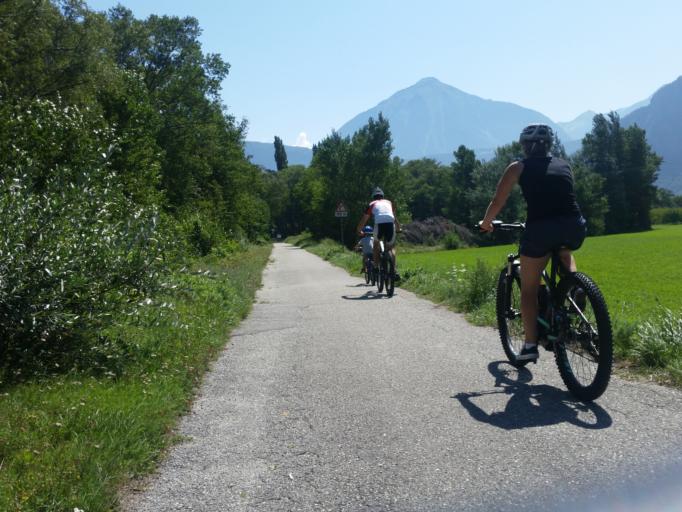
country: CH
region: Valais
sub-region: Saint-Maurice District
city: Vernayaz
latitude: 46.1385
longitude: 7.0499
